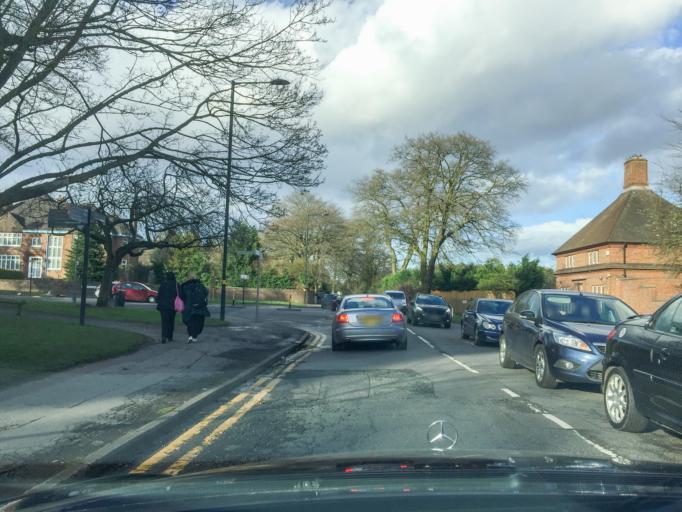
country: GB
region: England
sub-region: City and Borough of Birmingham
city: Birmingham
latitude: 52.4516
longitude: -1.9263
